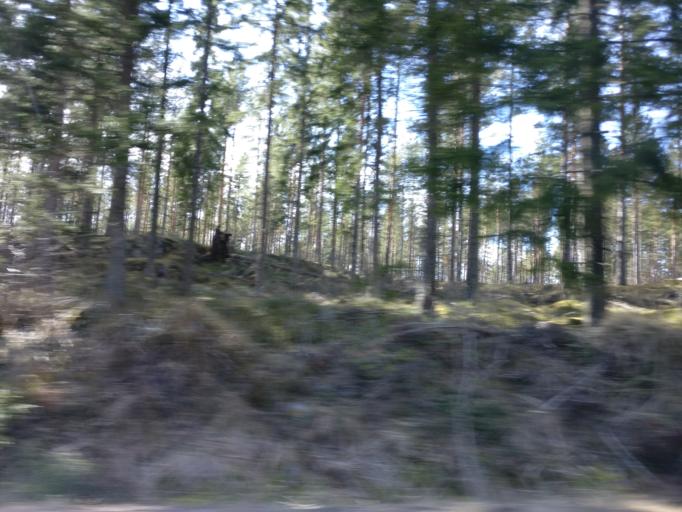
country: FI
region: Varsinais-Suomi
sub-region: Salo
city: Suomusjaervi
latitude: 60.3373
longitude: 23.6507
